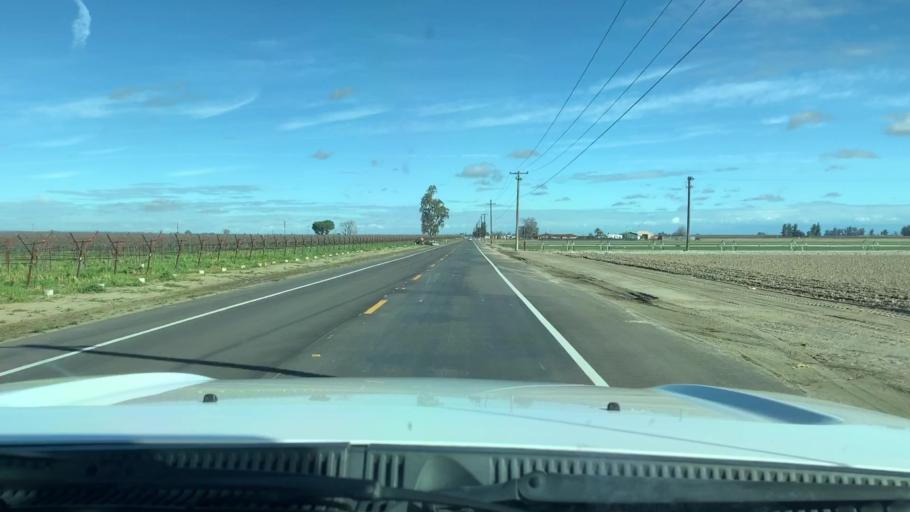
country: US
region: California
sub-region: Fresno County
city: Laton
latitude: 36.5067
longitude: -119.6830
